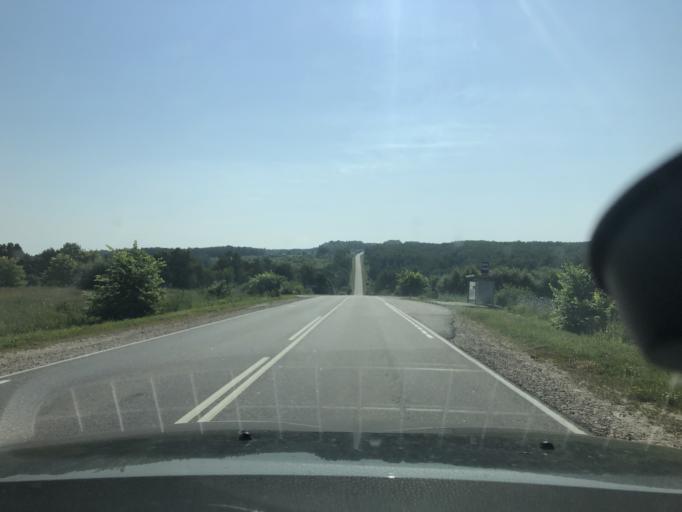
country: RU
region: Tula
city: Dubna
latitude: 54.1311
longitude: 37.0398
